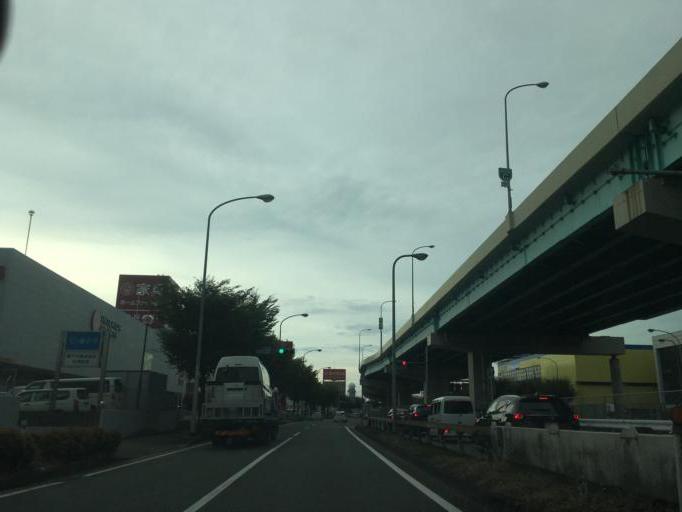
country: JP
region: Fukuoka
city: Fukuoka-shi
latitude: 33.5924
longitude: 130.4365
